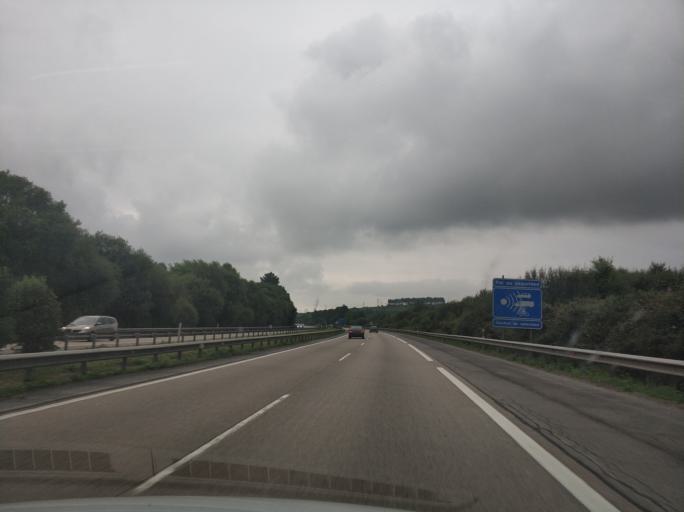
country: ES
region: Asturias
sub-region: Province of Asturias
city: Corvera de Asturias
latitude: 43.5213
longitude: -5.8230
